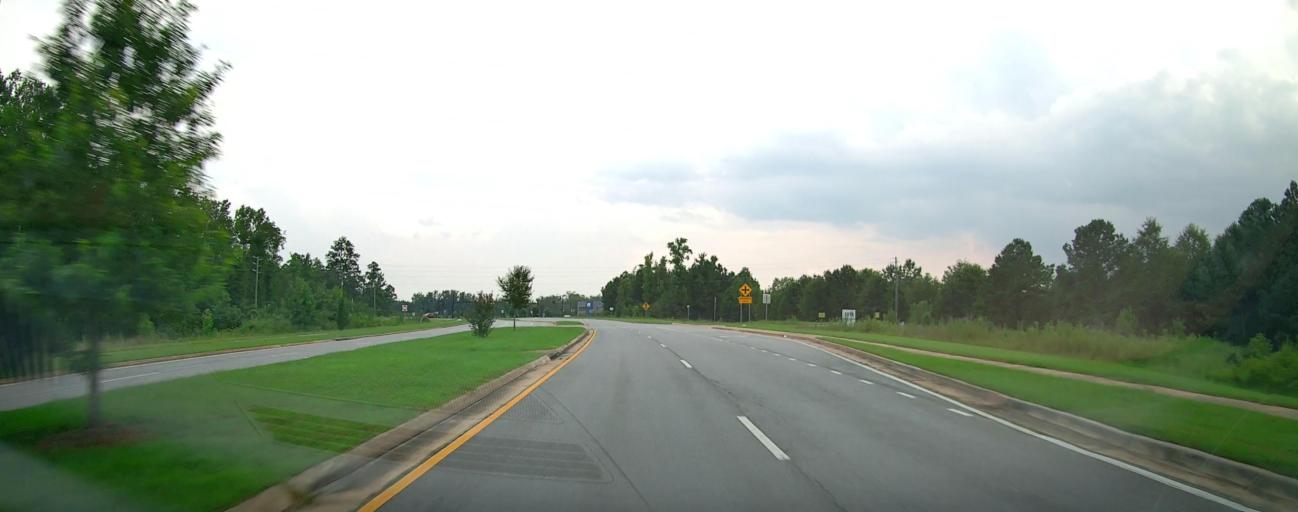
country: US
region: Georgia
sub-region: Muscogee County
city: Columbus
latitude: 32.5340
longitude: -84.8409
